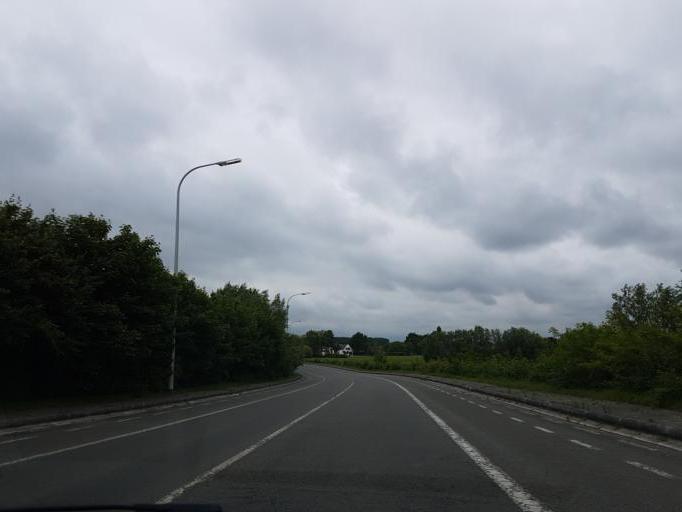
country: BE
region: Flanders
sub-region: Provincie Oost-Vlaanderen
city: Zomergem
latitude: 51.0956
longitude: 3.5733
